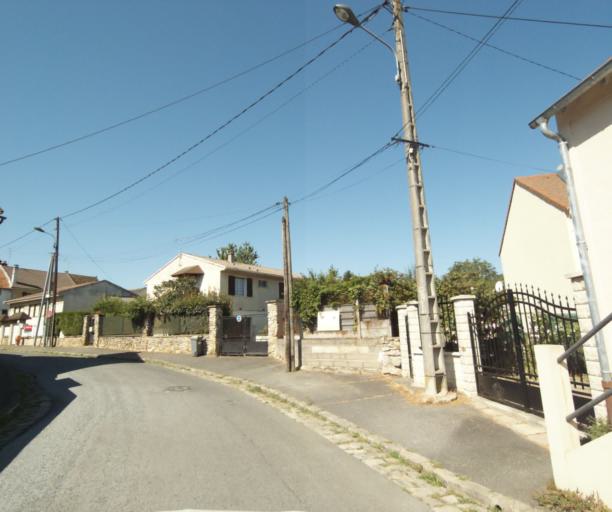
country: FR
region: Ile-de-France
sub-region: Departement de l'Essonne
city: Itteville
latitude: 48.5141
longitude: 2.3374
